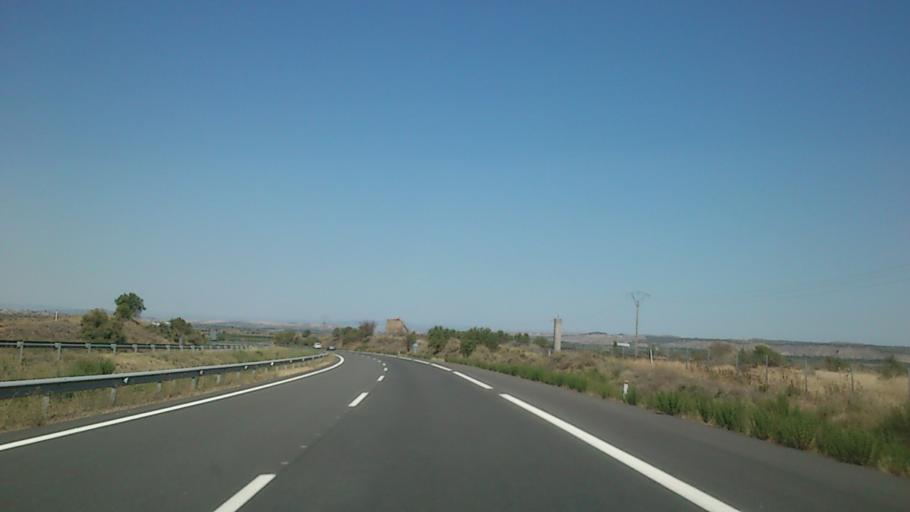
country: ES
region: La Rioja
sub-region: Provincia de La Rioja
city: Aldeanueva de Ebro
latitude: 42.2432
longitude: -1.9011
